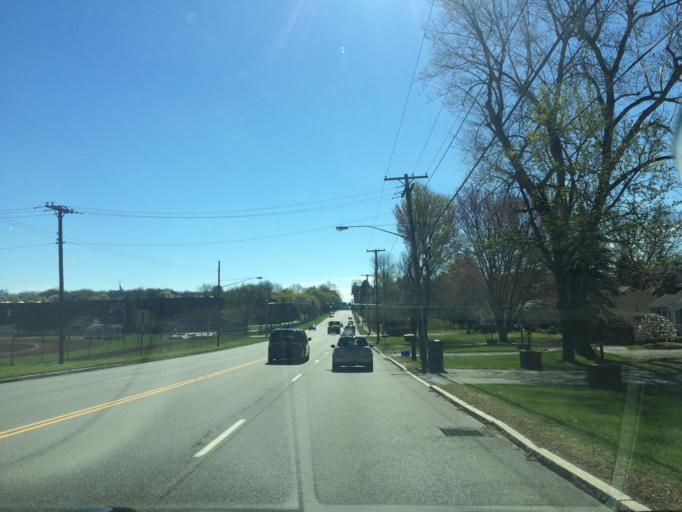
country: US
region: New York
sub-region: Monroe County
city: East Rochester
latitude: 43.1070
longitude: -77.4961
